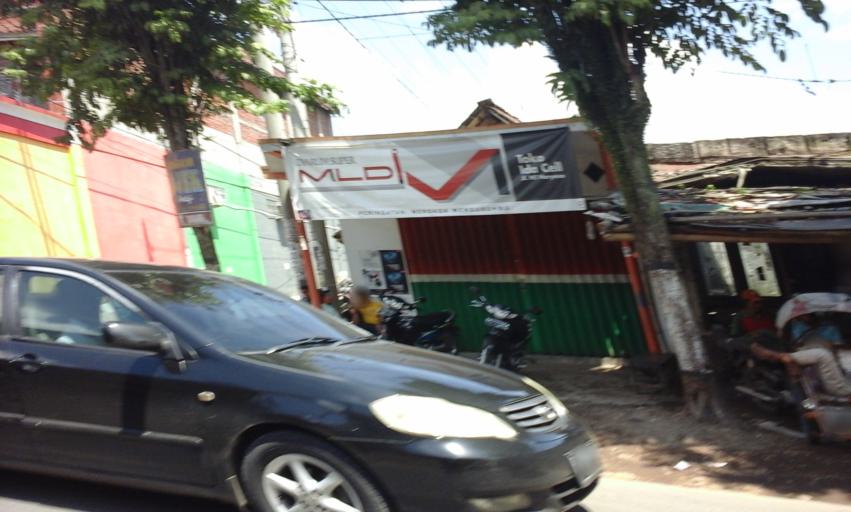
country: ID
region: East Java
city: Sumberketangi
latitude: -8.1871
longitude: 113.7457
